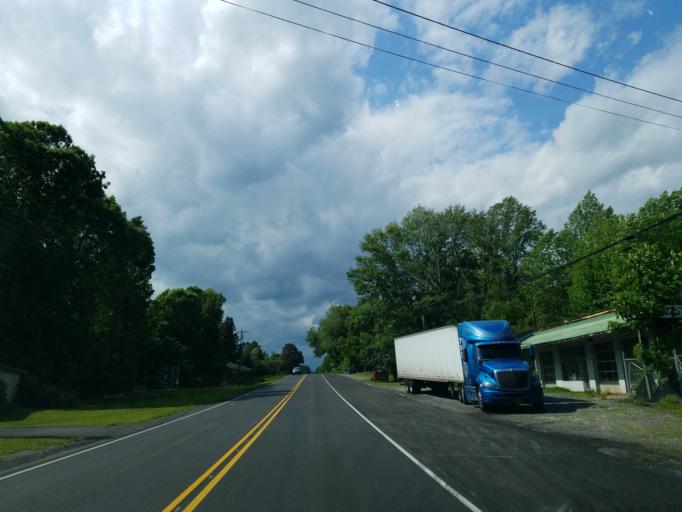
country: US
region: Georgia
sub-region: Pickens County
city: Jasper
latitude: 34.4358
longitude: -84.3964
